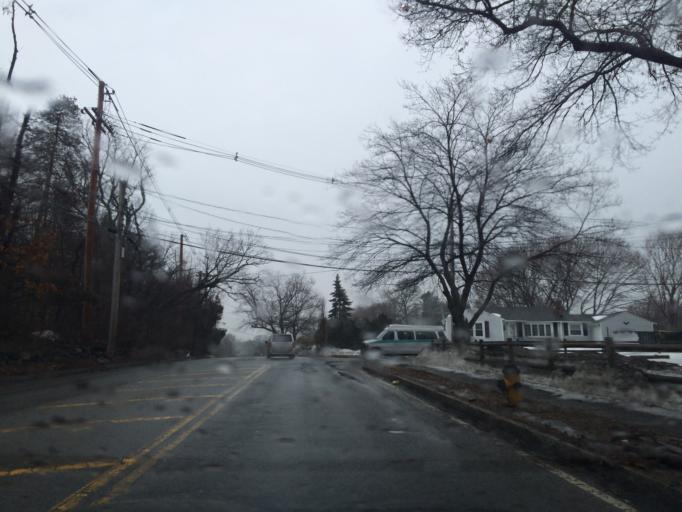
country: US
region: Massachusetts
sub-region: Middlesex County
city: Waltham
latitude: 42.4078
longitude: -71.2241
